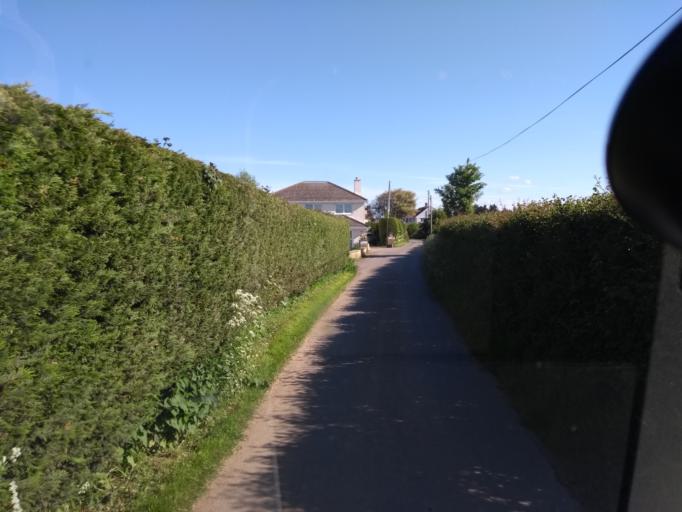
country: GB
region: England
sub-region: Somerset
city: Bridgwater
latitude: 51.1427
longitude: -3.0353
